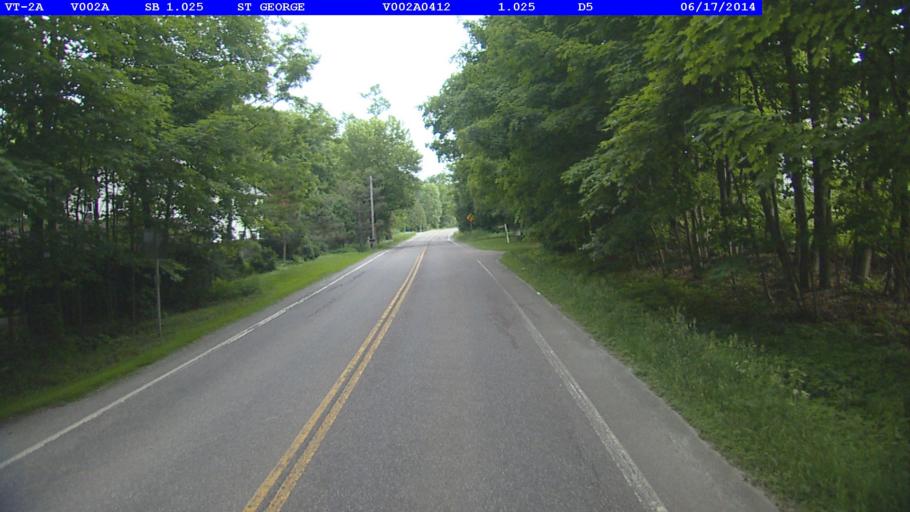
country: US
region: Vermont
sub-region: Chittenden County
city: Hinesburg
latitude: 44.3842
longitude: -73.1272
